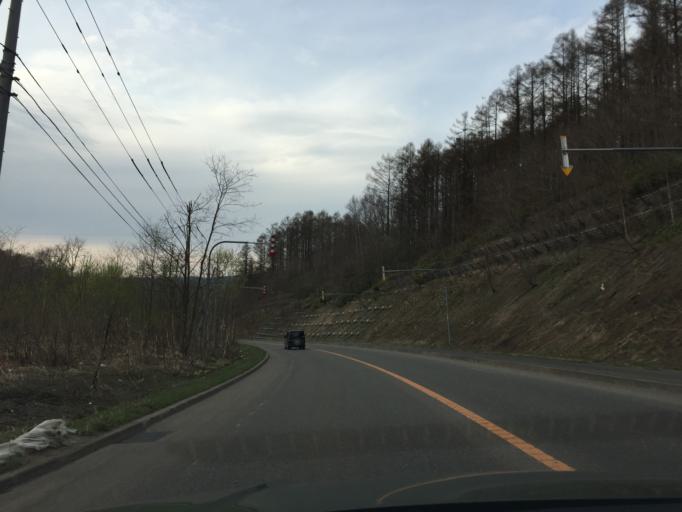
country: JP
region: Hokkaido
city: Utashinai
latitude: 43.5326
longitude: 142.0678
